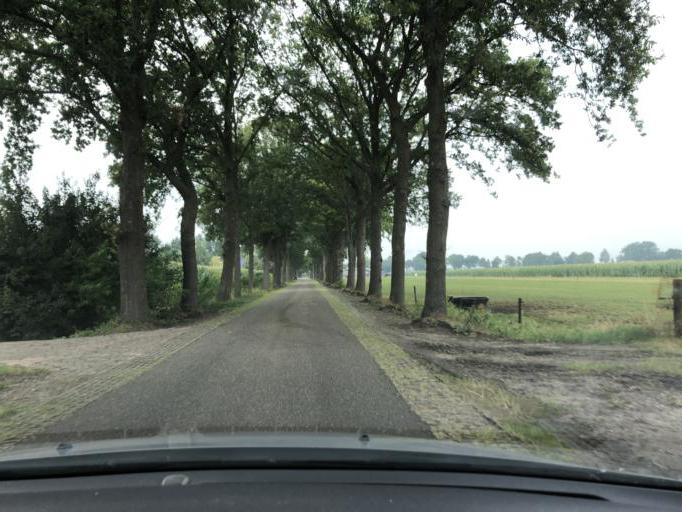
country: NL
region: Overijssel
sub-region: Gemeente Dalfsen
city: Dalfsen
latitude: 52.5868
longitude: 6.2942
